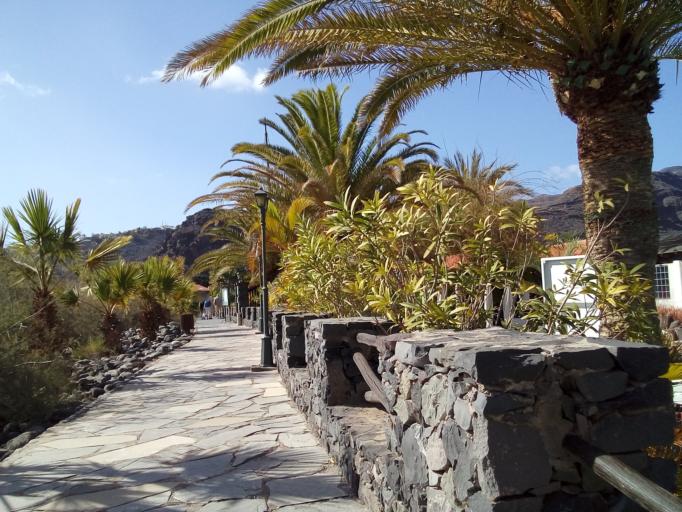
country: ES
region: Canary Islands
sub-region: Provincia de Santa Cruz de Tenerife
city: Alajero
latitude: 28.0300
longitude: -17.1910
